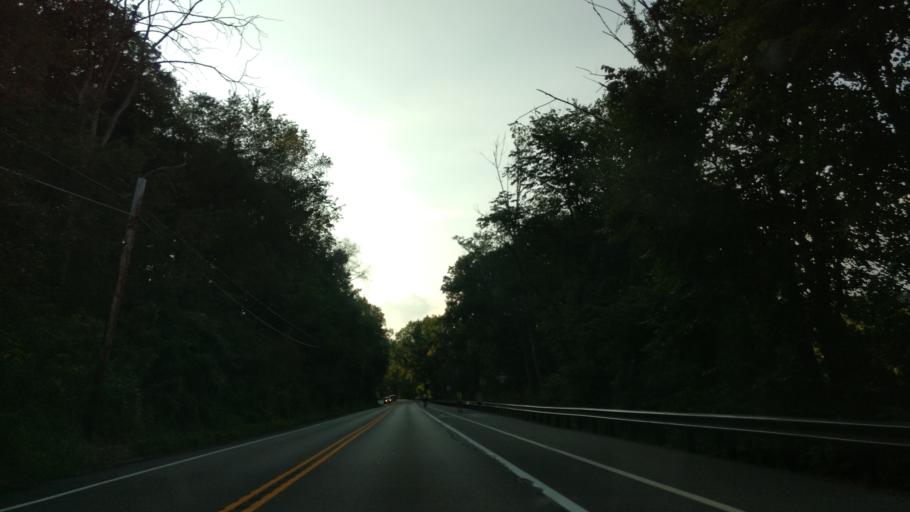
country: US
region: Pennsylvania
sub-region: Allegheny County
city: Gibsonia
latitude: 40.5928
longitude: -80.0049
